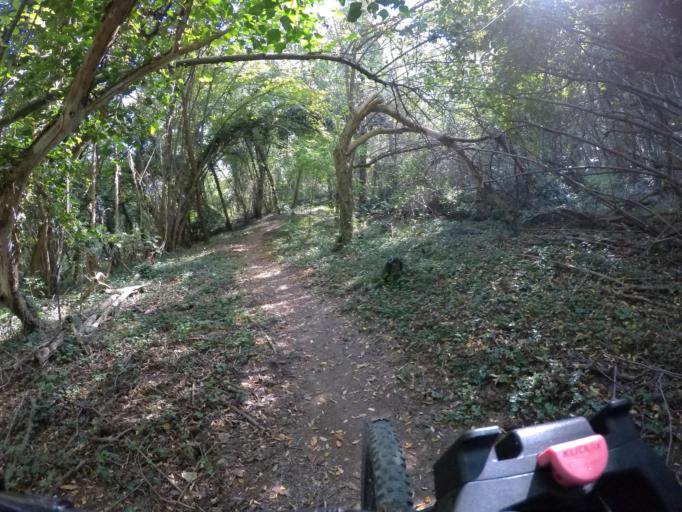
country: IT
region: Friuli Venezia Giulia
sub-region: Provincia di Udine
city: Manzano
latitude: 45.9964
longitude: 13.3844
